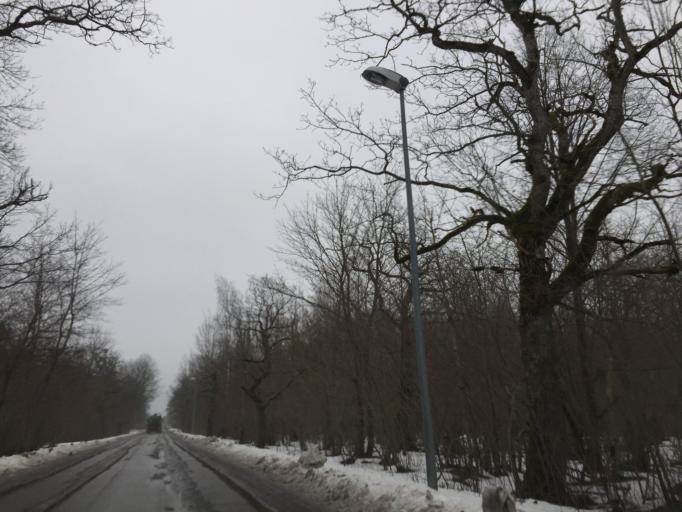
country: EE
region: Saare
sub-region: Kuressaare linn
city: Kuressaare
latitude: 58.2634
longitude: 22.5247
